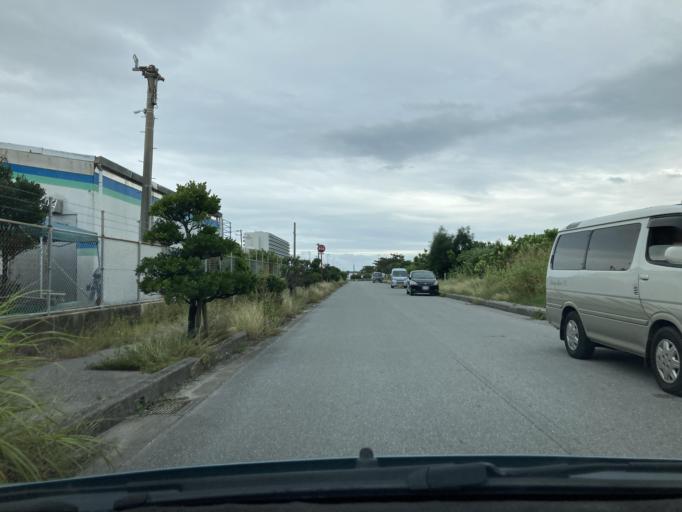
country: JP
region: Okinawa
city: Itoman
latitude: 26.1365
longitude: 127.6508
